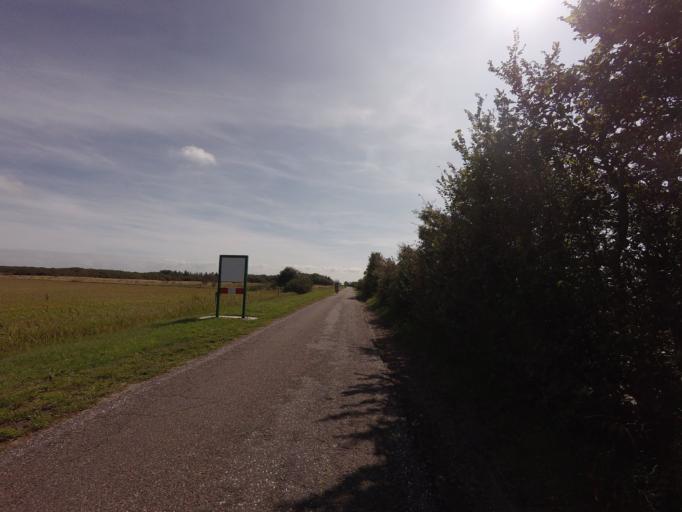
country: NL
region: Friesland
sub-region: Gemeente Ameland
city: Hollum
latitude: 53.4457
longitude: 5.6617
